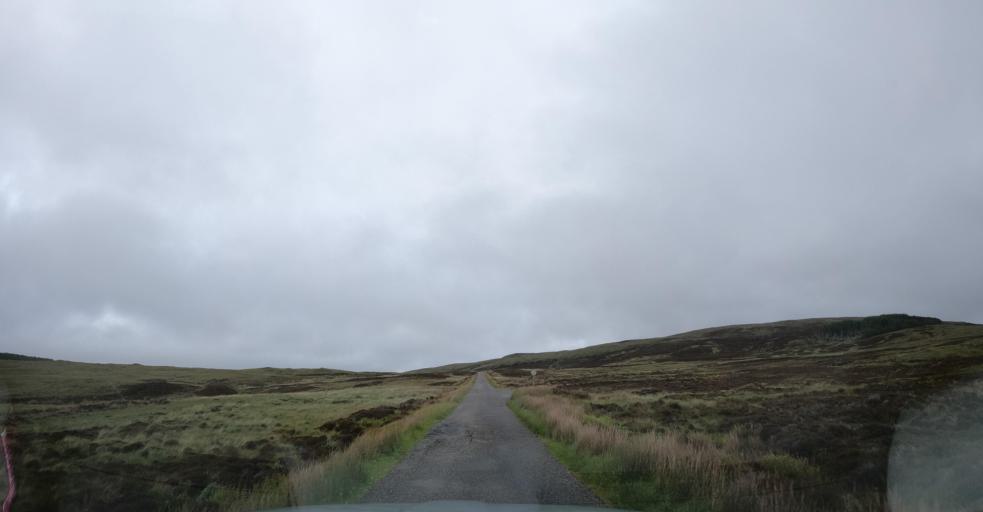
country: GB
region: Scotland
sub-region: Eilean Siar
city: Isle of North Uist
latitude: 57.6073
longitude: -7.3768
